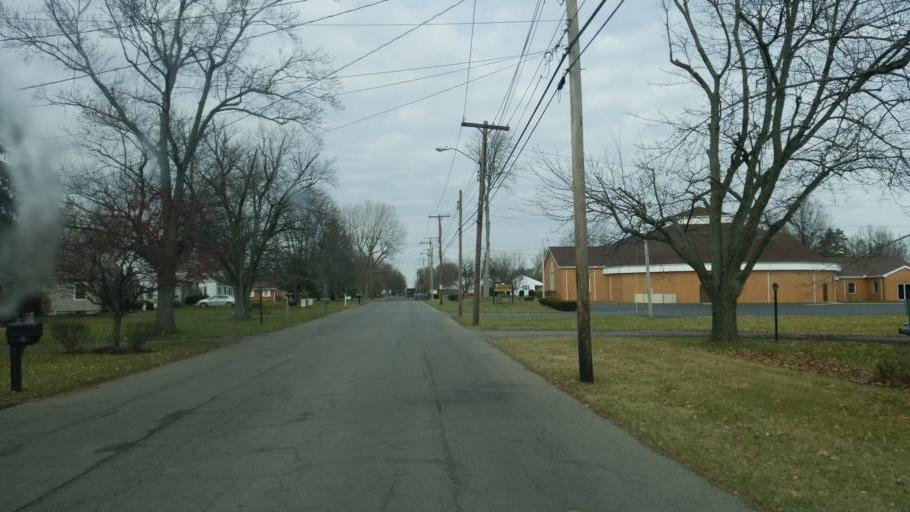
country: US
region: Ohio
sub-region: Crawford County
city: Galion
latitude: 40.7420
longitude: -82.7832
